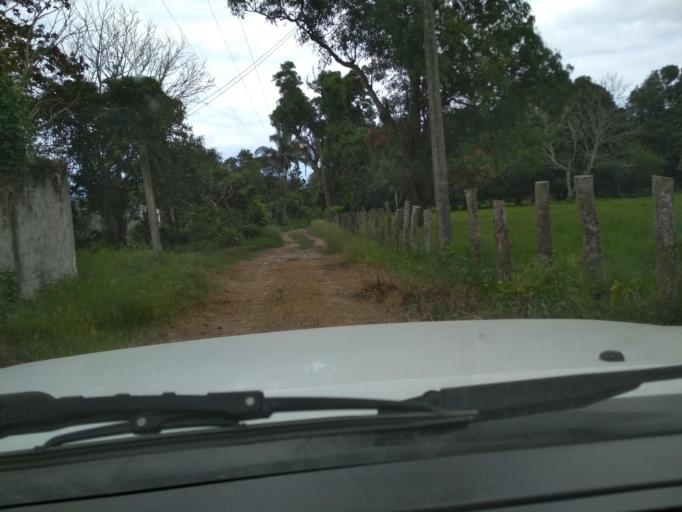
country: MX
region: Veracruz
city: El Tejar
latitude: 19.0621
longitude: -96.1559
